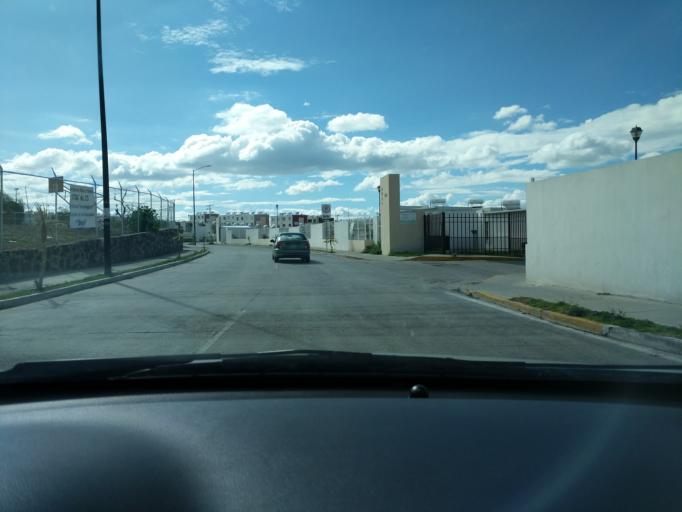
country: MX
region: Queretaro
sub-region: El Marques
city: La Loma
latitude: 20.5856
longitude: -100.2616
